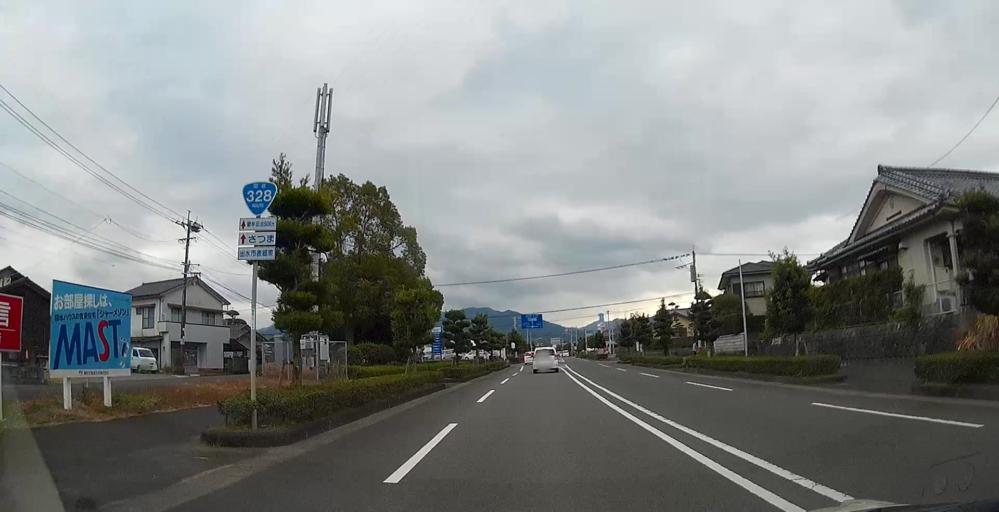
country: JP
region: Kagoshima
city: Izumi
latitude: 32.0837
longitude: 130.3443
